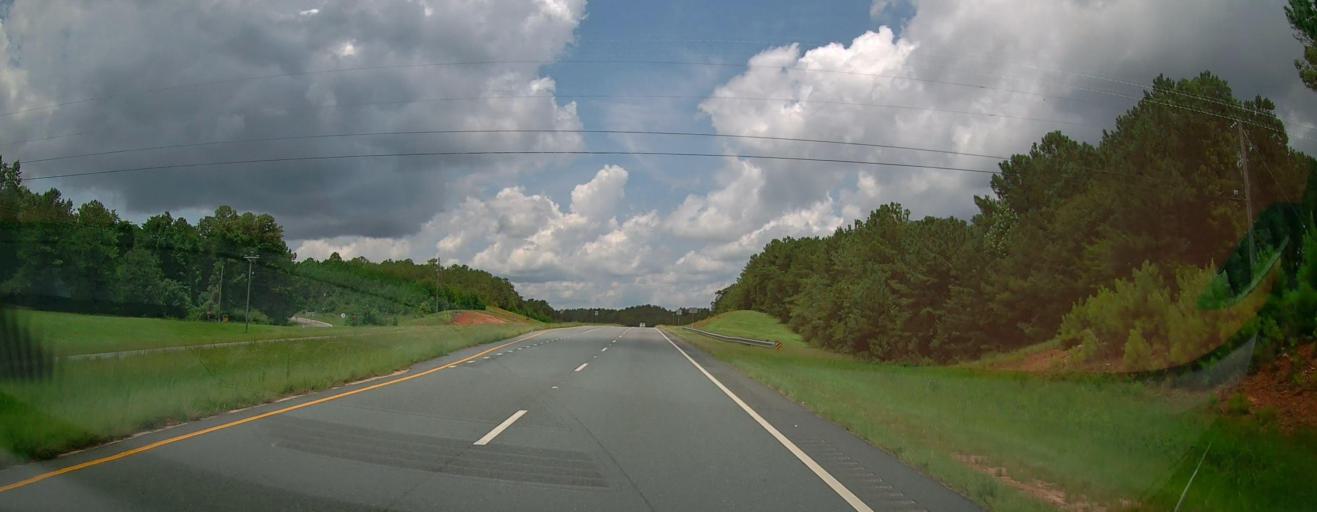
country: US
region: Georgia
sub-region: Upson County
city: Thomaston
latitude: 32.8302
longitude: -84.3080
